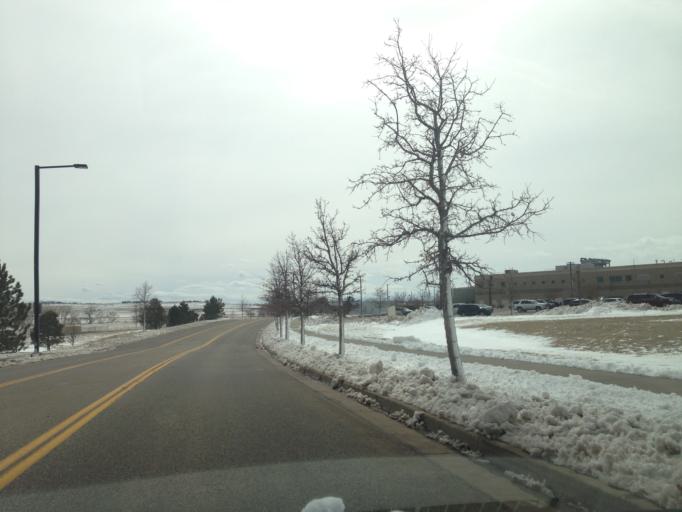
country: US
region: Colorado
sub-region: Boulder County
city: Lafayette
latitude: 39.9705
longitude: -105.0830
